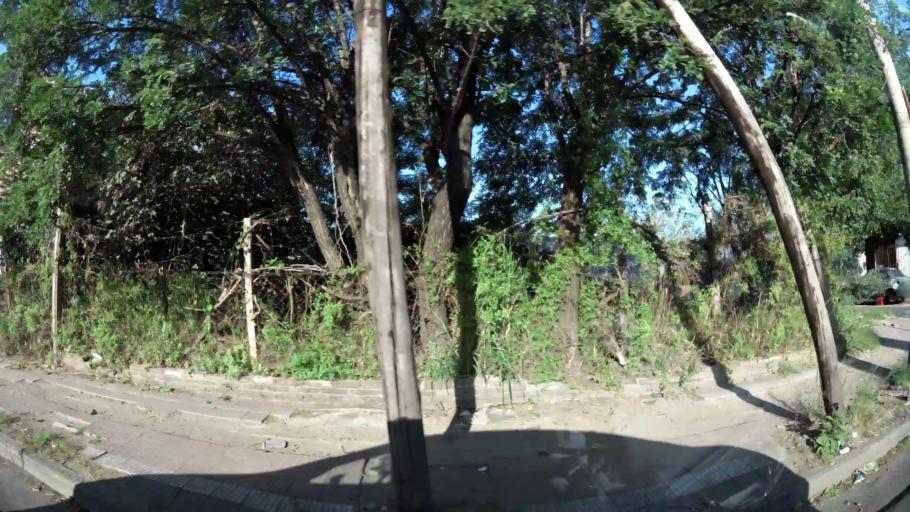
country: AR
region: Cordoba
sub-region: Departamento de Capital
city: Cordoba
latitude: -31.4367
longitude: -64.2480
